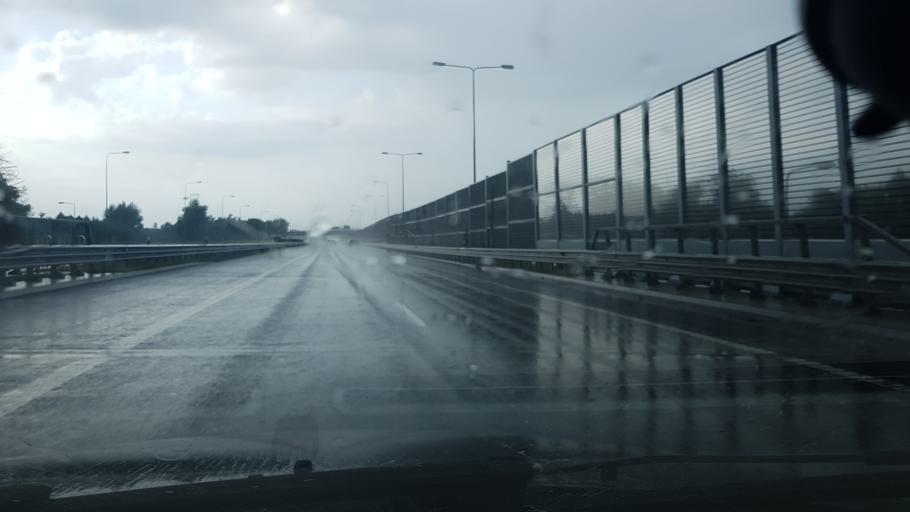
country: PL
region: Warmian-Masurian Voivodeship
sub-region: Powiat olsztynski
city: Olsztynek
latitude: 53.4957
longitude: 20.3156
